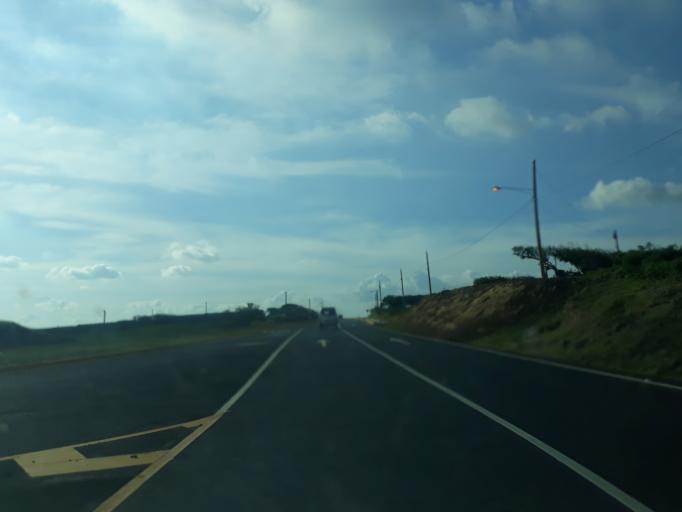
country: NI
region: Managua
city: El Crucero
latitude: 11.9368
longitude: -86.2938
